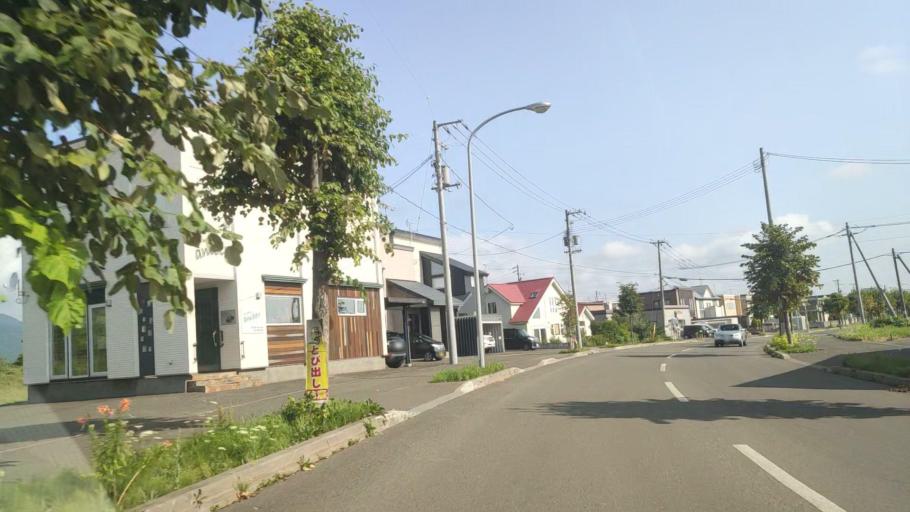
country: JP
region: Hokkaido
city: Shimo-furano
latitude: 43.3475
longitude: 142.3762
